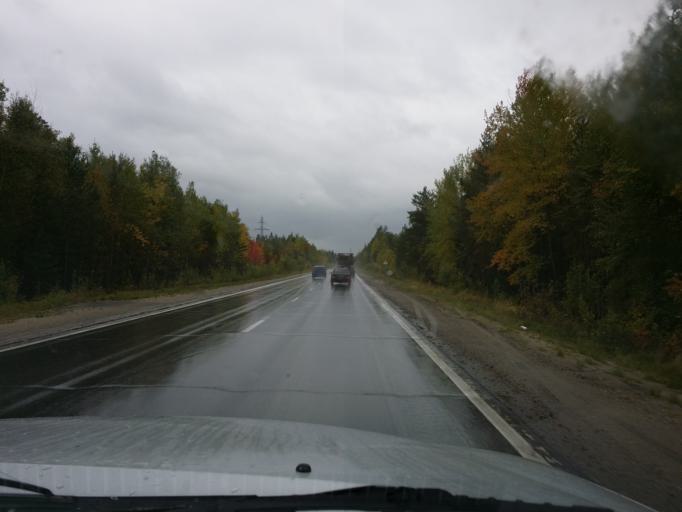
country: RU
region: Khanty-Mansiyskiy Avtonomnyy Okrug
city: Megion
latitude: 61.1484
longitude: 75.7490
